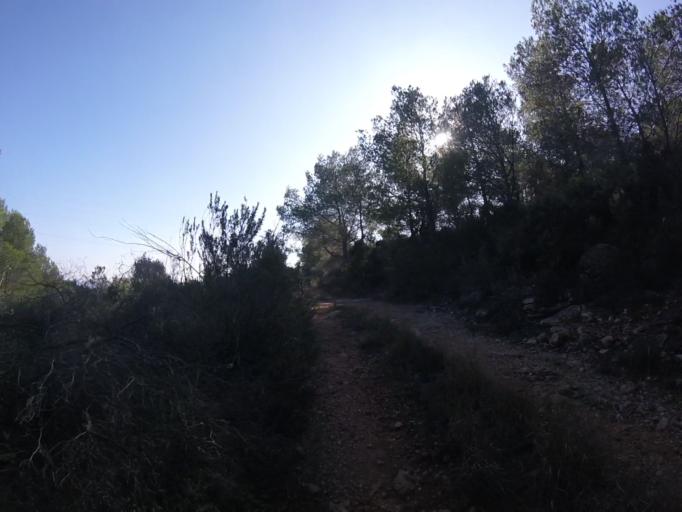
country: ES
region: Valencia
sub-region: Provincia de Castello
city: Alcoceber
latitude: 40.2905
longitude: 0.3173
